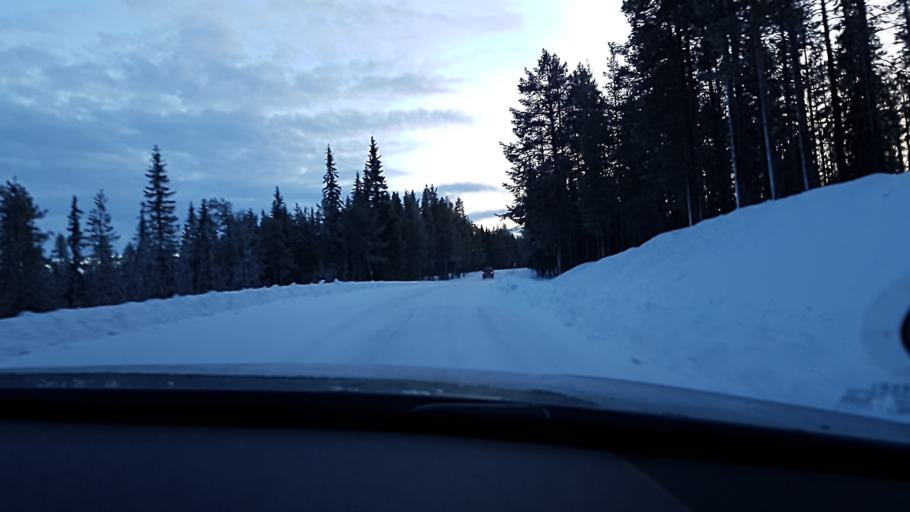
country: SE
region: Vaesterbotten
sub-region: Sorsele Kommun
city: Sorsele
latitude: 65.4997
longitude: 17.5560
